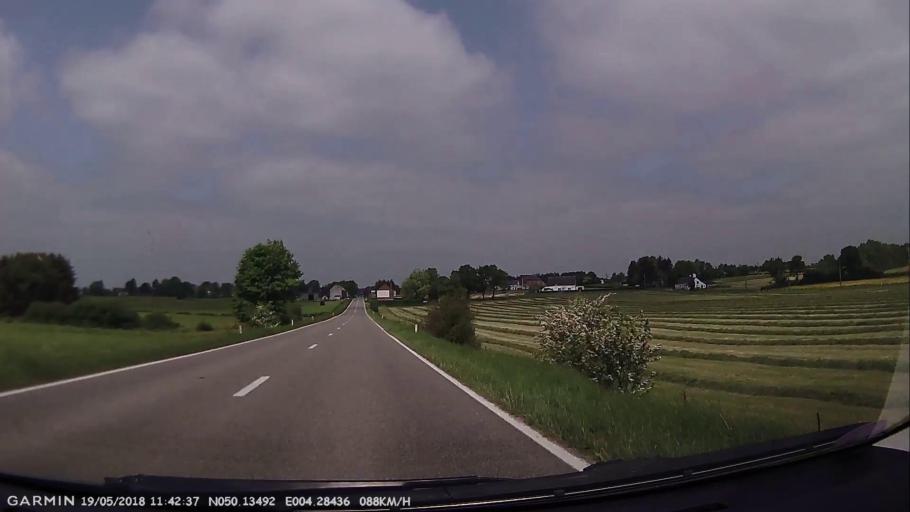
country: BE
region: Wallonia
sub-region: Province du Hainaut
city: Froidchapelle
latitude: 50.1352
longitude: 4.2841
